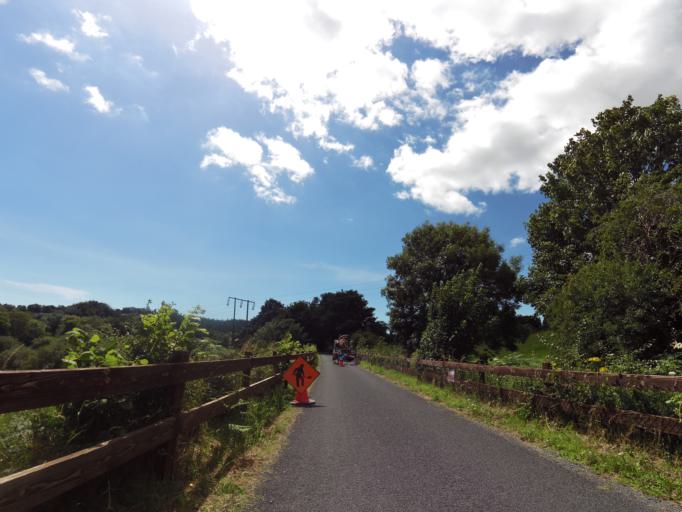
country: IE
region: Leinster
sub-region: Kilkenny
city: Mooncoin
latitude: 52.2441
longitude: -7.2622
